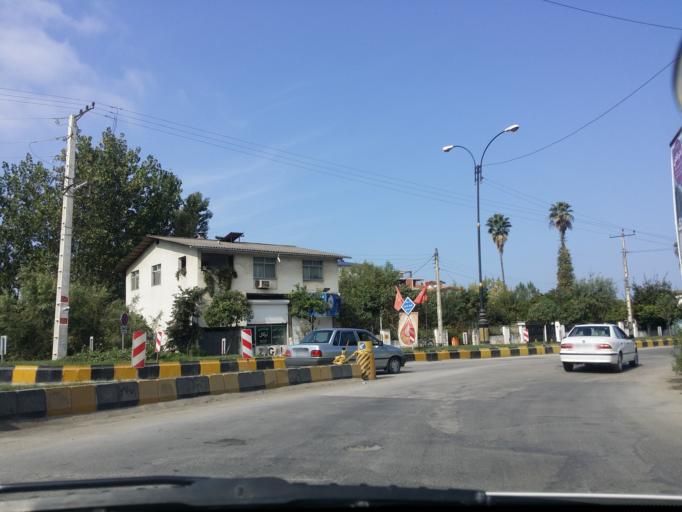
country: IR
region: Mazandaran
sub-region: Nowshahr
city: Nowshahr
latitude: 36.6382
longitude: 51.4894
